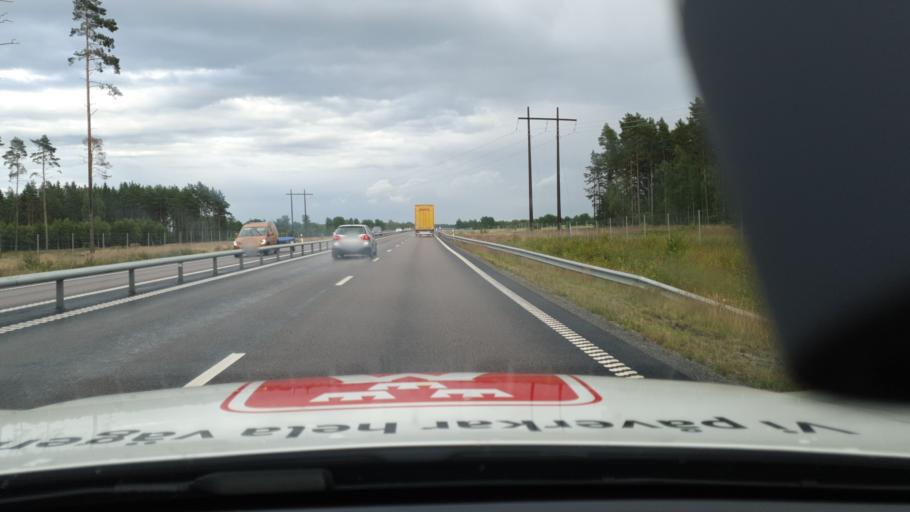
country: SE
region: Vaestra Goetaland
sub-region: Lidkopings Kommun
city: Lidkoping
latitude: 58.4797
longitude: 13.2113
